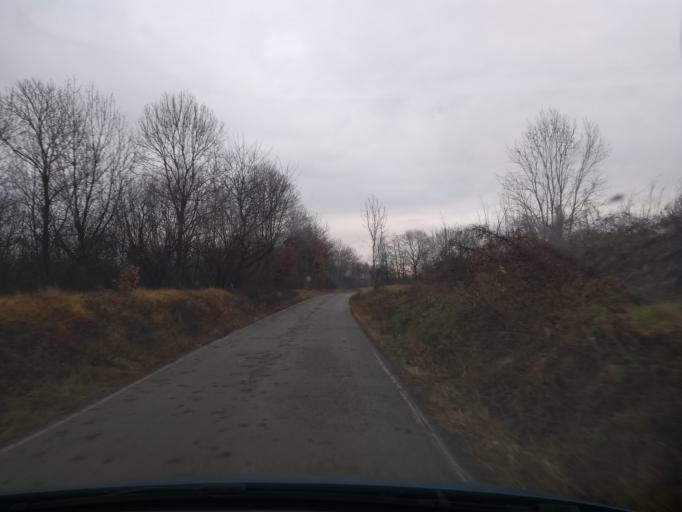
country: IT
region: Piedmont
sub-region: Provincia di Torino
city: Barbania
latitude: 45.2769
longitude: 7.6434
